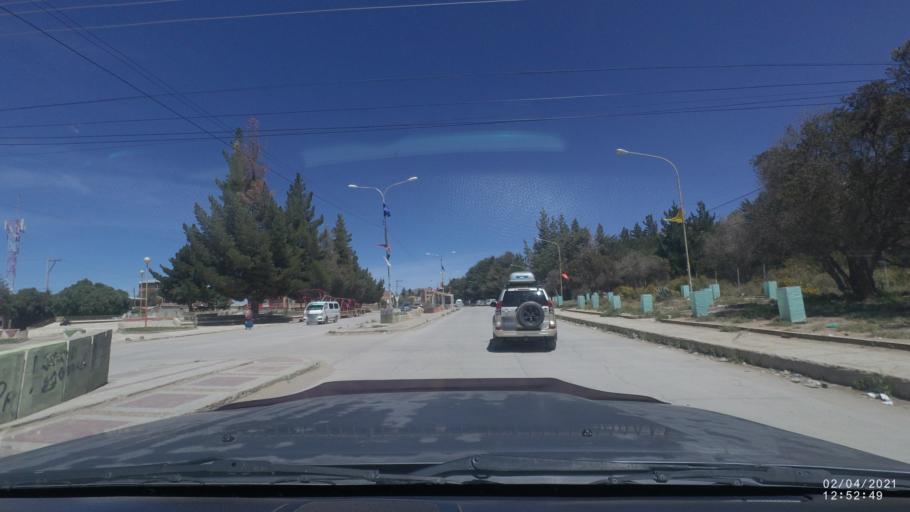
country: BO
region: Oruro
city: Oruro
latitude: -17.9883
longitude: -67.1347
